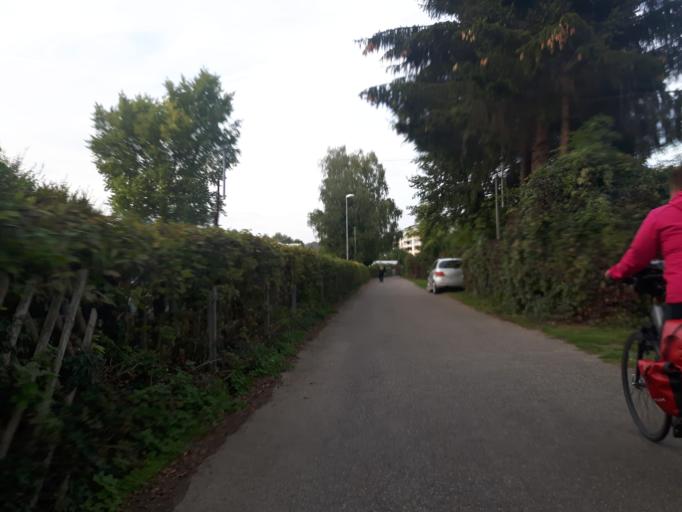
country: DE
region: Rheinland-Pfalz
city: Bad Honningen
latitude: 50.5088
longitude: 7.3111
